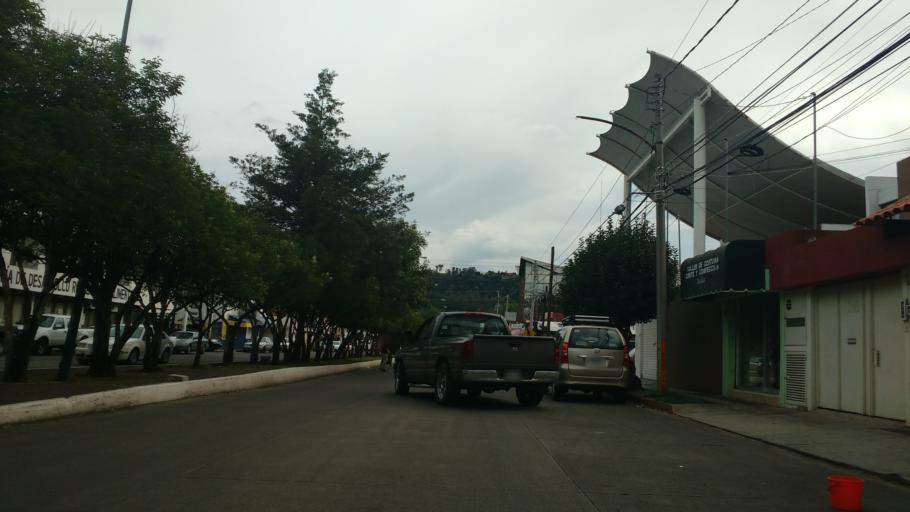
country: MX
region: Michoacan
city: Morelia
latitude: 19.6899
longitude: -101.1723
